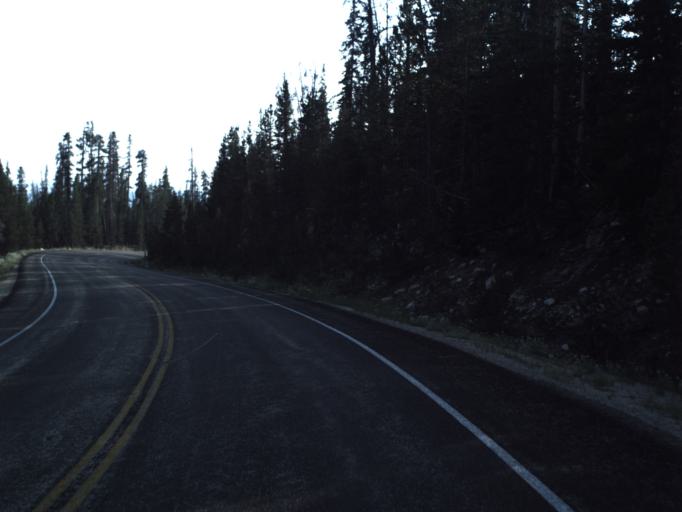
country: US
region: Utah
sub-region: Summit County
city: Kamas
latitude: 40.6763
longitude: -110.9463
